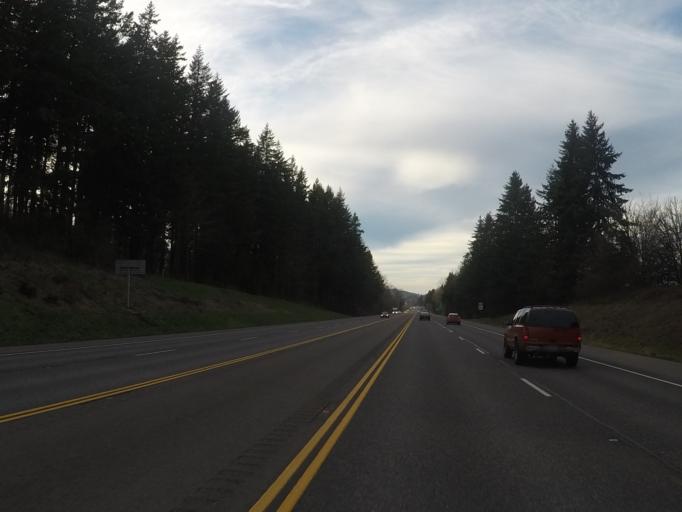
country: US
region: Oregon
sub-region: Clackamas County
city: Sandy
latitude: 45.4203
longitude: -122.3225
